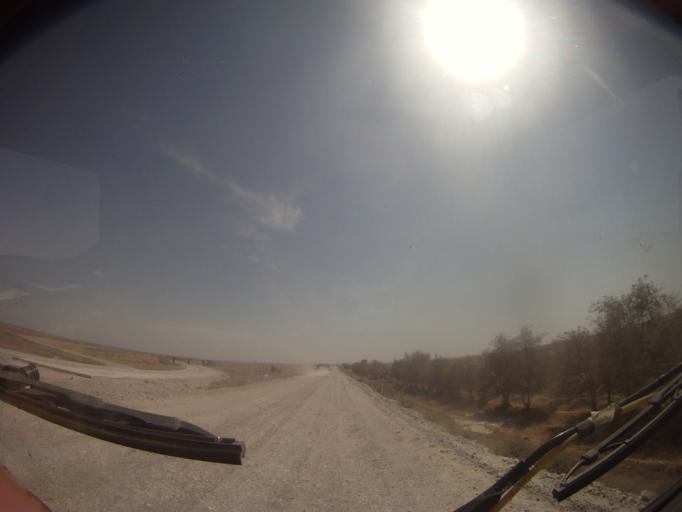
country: KZ
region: Ongtustik Qazaqstan
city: Temirlanovka
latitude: 42.6511
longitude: 69.2358
